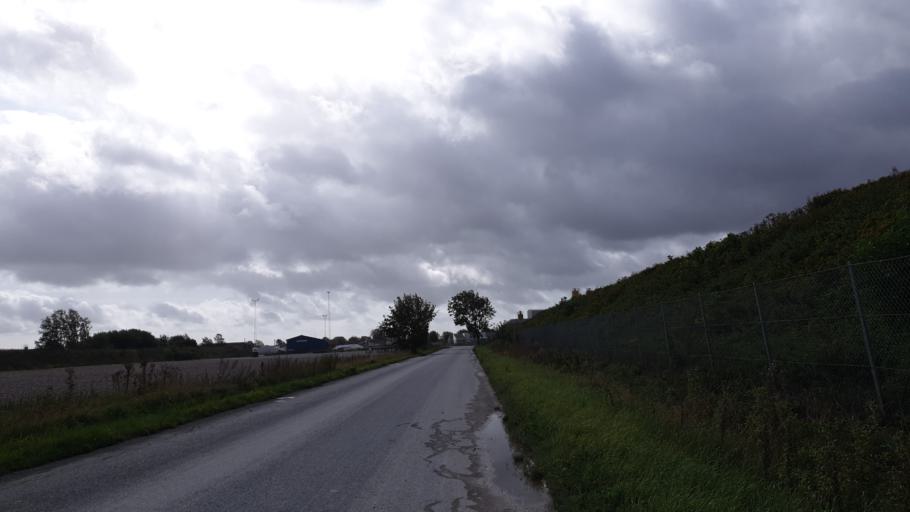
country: DK
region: Central Jutland
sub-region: Hedensted Kommune
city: Hedensted
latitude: 55.8126
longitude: 9.6854
